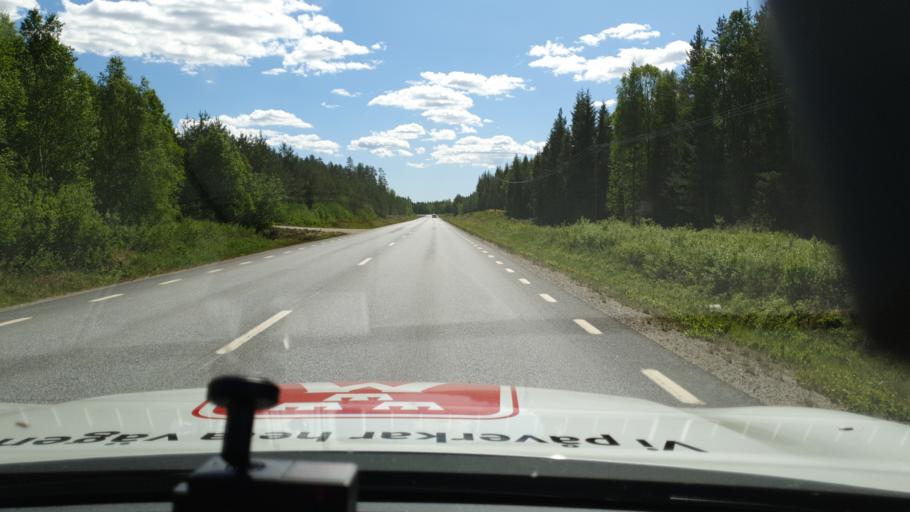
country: SE
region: Vaesterbotten
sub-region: Vannas Kommun
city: Vaennaes
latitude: 64.0189
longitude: 19.6923
